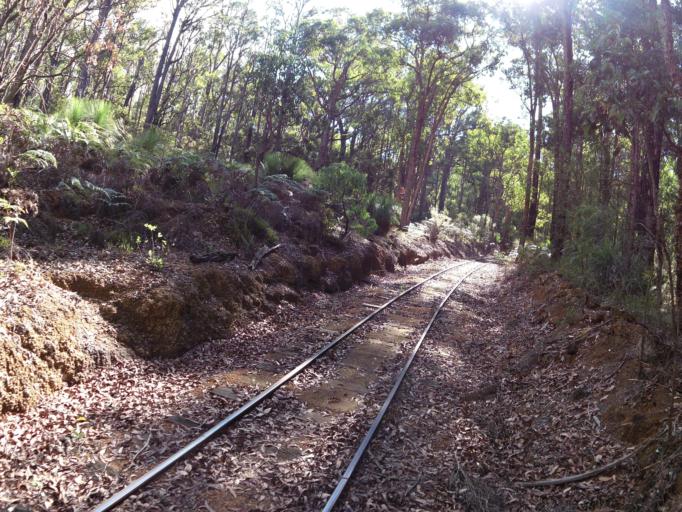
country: AU
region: Western Australia
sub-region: Waroona
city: Waroona
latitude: -32.7259
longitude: 116.1101
